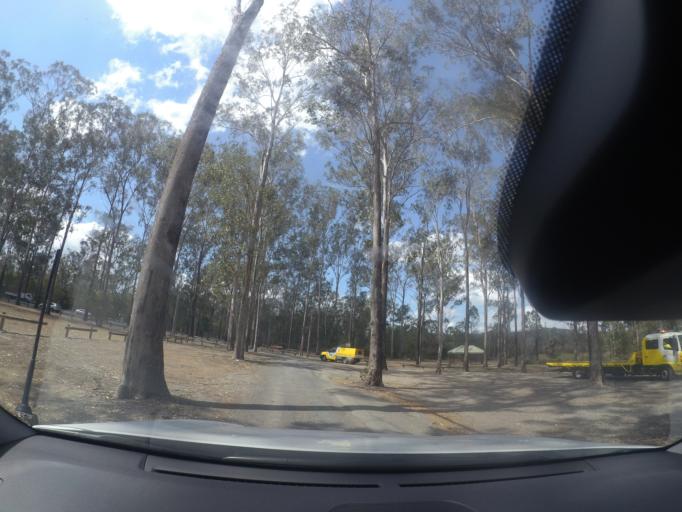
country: AU
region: Queensland
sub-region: Logan
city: Logan City
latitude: -27.6635
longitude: 153.1212
